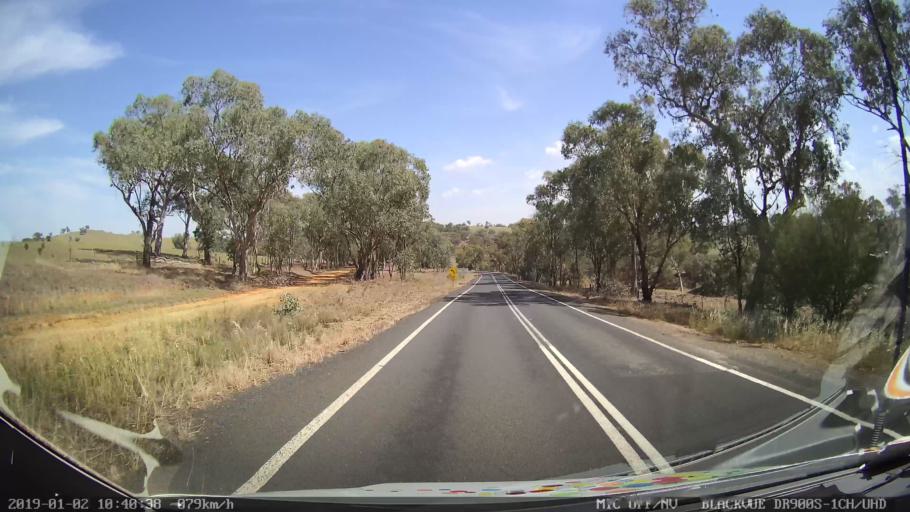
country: AU
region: New South Wales
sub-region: Cootamundra
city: Cootamundra
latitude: -34.8001
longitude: 148.3142
